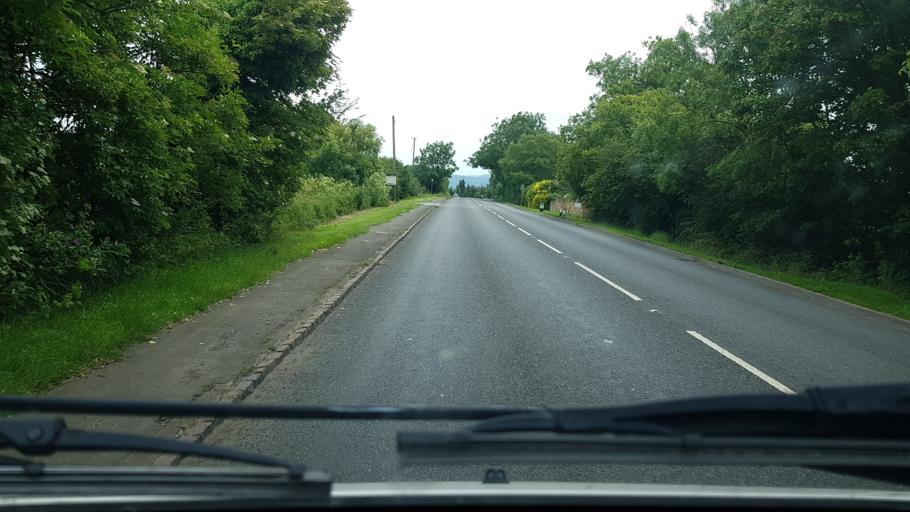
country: GB
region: England
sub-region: Worcestershire
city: Badsey
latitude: 52.0620
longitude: -1.8913
